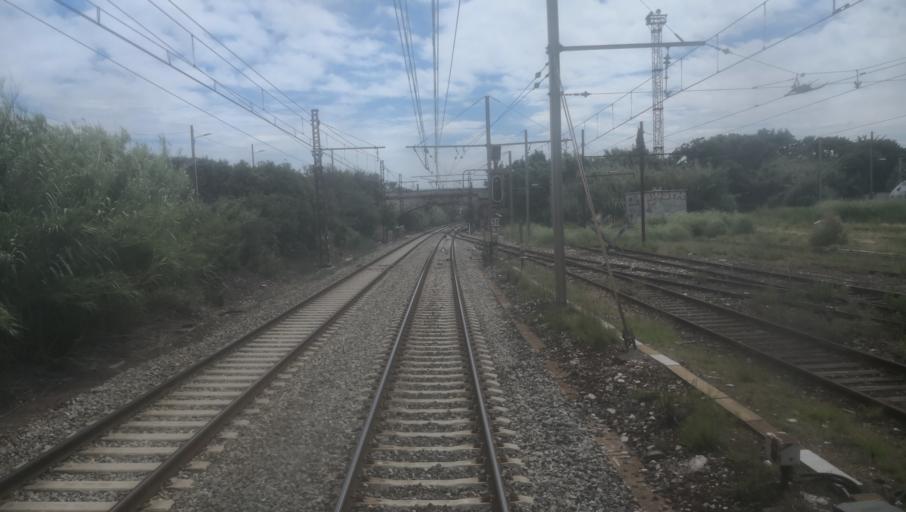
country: FR
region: Languedoc-Roussillon
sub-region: Departement de l'Herault
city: Montpellier
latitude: 43.5869
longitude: 3.8766
